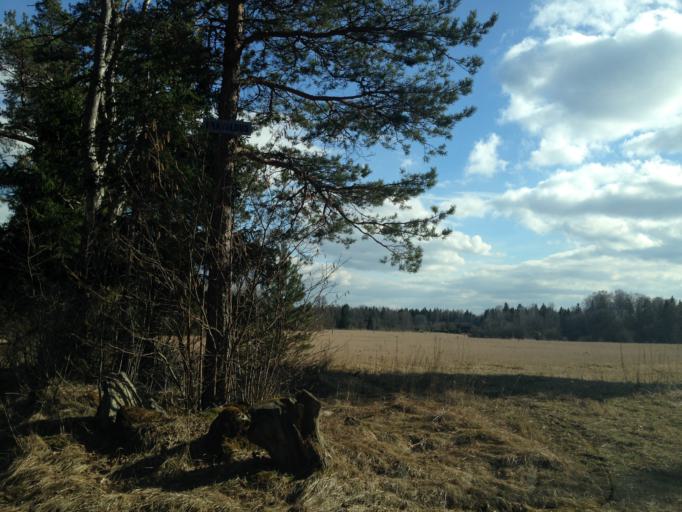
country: EE
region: Harju
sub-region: Keila linn
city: Keila
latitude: 59.1780
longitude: 24.4454
